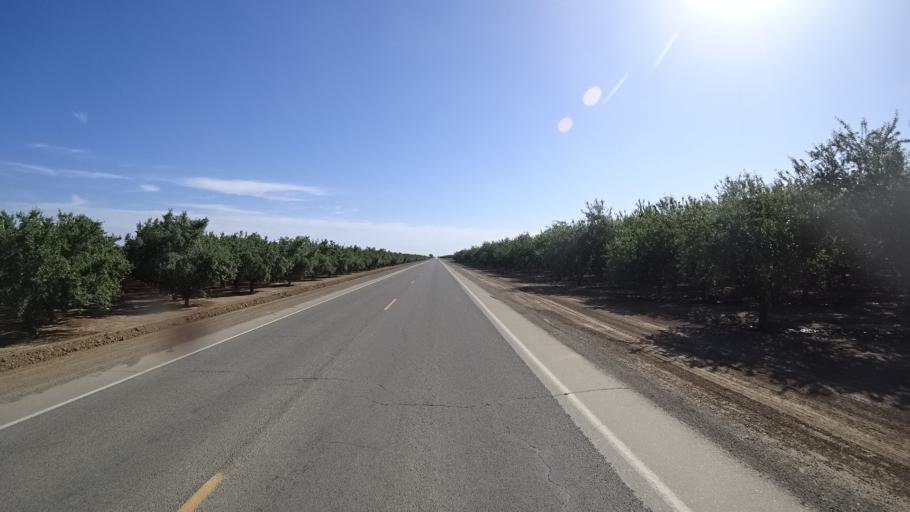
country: US
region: California
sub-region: Fresno County
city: Huron
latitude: 36.1115
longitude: -120.0448
